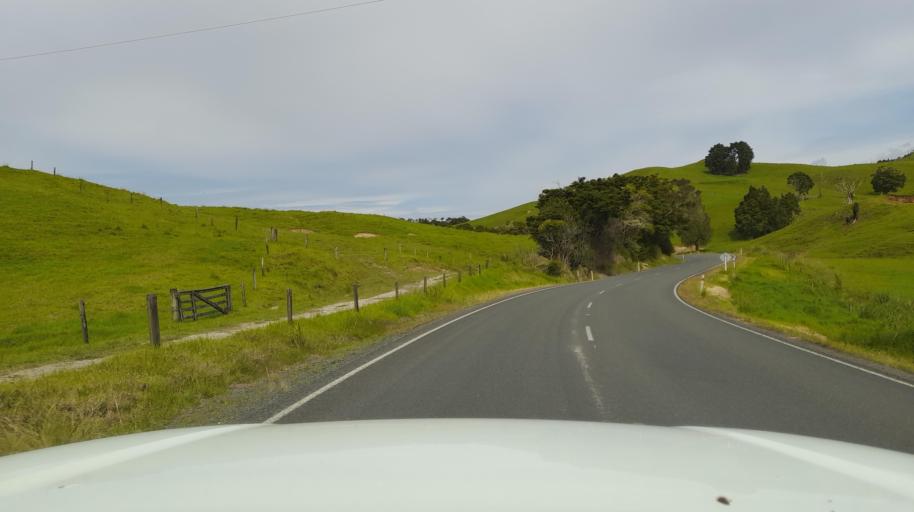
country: NZ
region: Northland
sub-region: Far North District
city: Kaitaia
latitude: -35.2699
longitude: 173.4891
